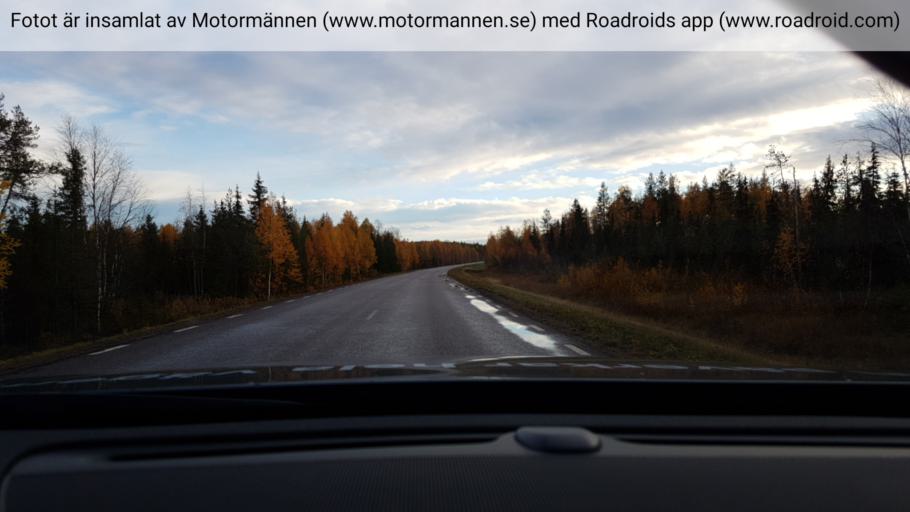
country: SE
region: Norrbotten
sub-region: Overkalix Kommun
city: OEverkalix
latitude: 66.8499
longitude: 22.7588
